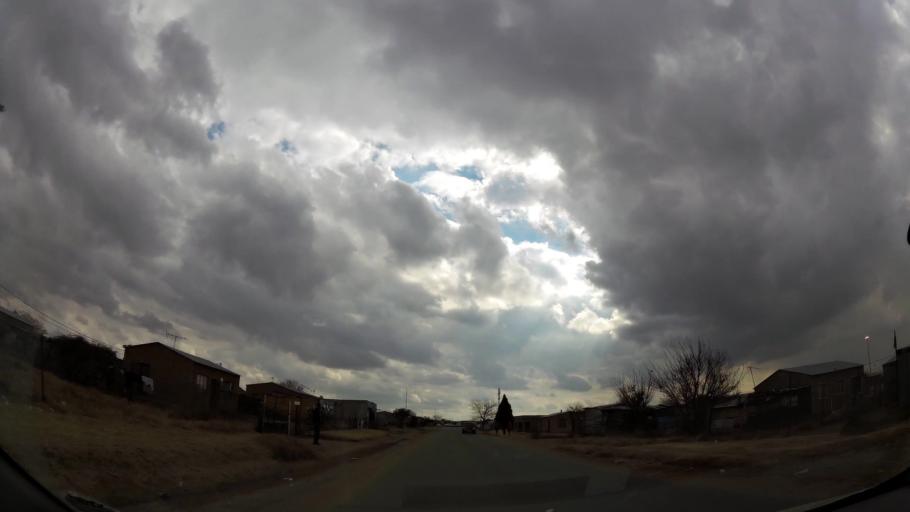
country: ZA
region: Orange Free State
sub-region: Fezile Dabi District Municipality
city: Sasolburg
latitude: -26.8571
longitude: 27.8774
